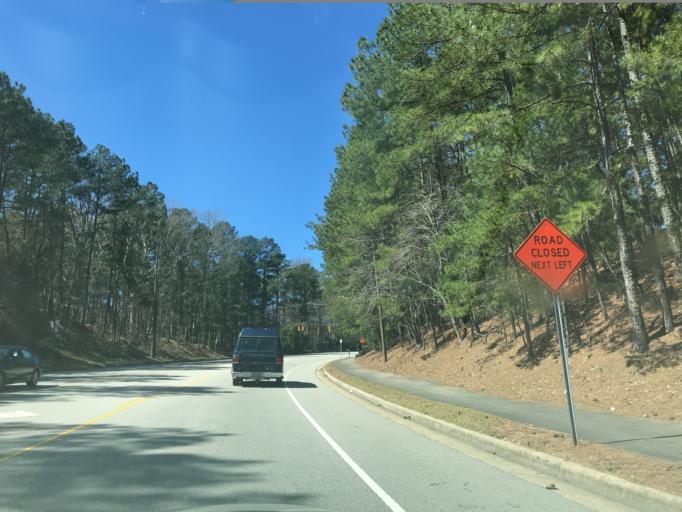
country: US
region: North Carolina
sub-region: Wake County
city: West Raleigh
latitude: 35.7666
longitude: -78.7037
